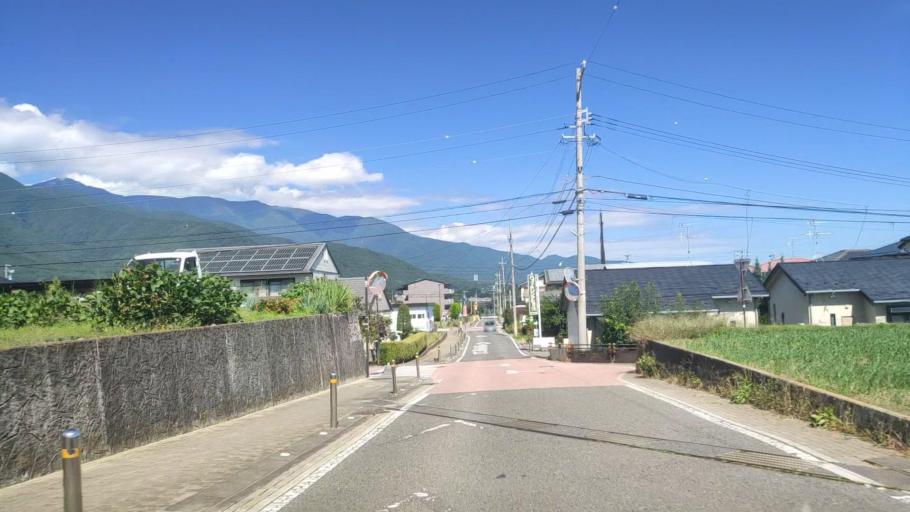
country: JP
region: Nagano
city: Toyoshina
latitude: 36.2003
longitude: 137.8605
